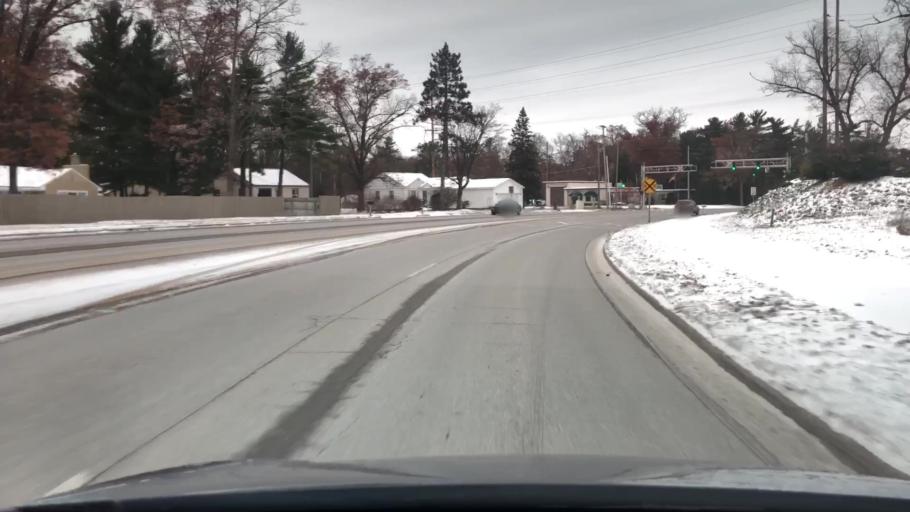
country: US
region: Michigan
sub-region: Grand Traverse County
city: Traverse City
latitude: 44.7446
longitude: -85.5610
